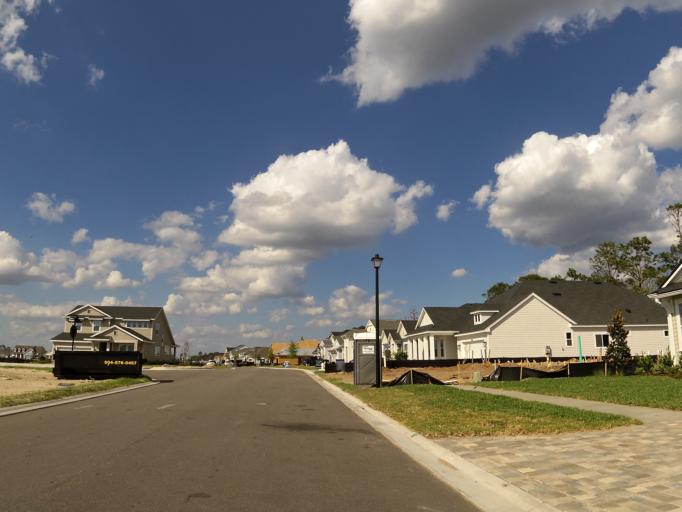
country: US
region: Florida
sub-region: Saint Johns County
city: Palm Valley
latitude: 30.1733
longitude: -81.5030
